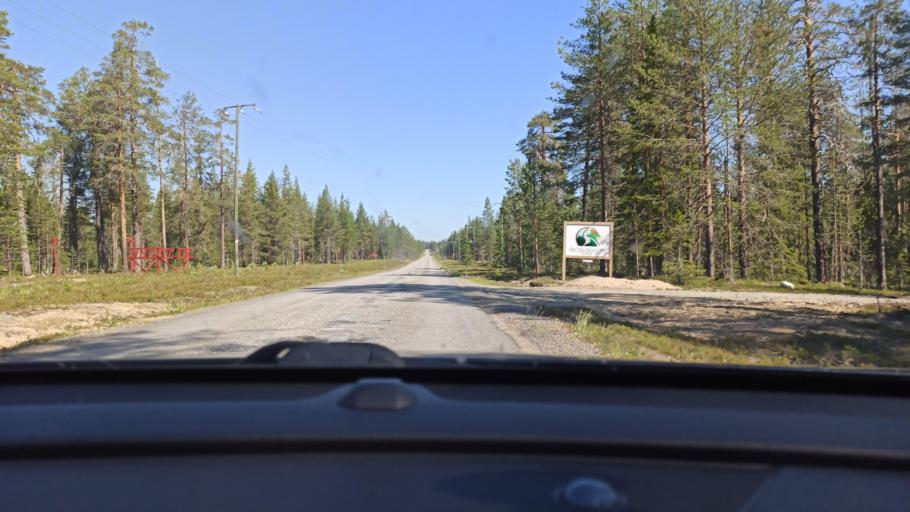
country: FI
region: Lapland
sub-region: Tunturi-Lappi
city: Kolari
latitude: 67.6453
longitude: 24.1598
